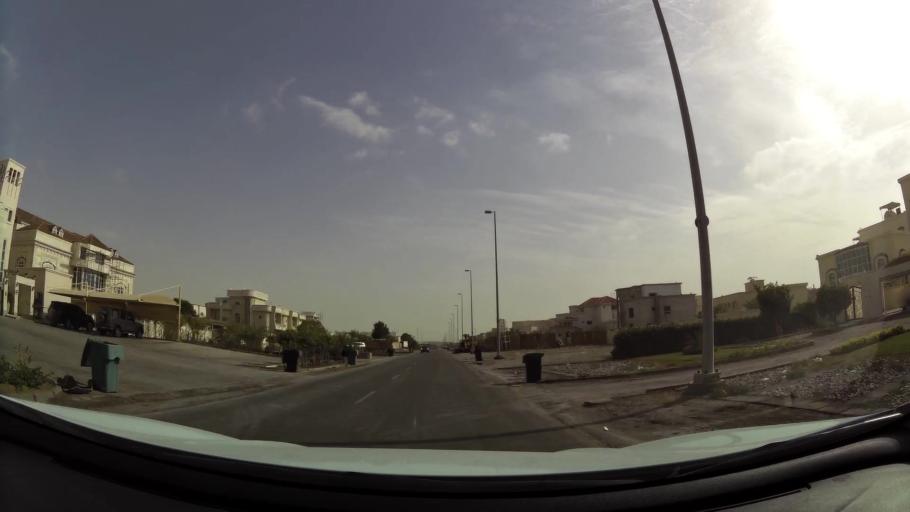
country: AE
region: Abu Dhabi
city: Abu Dhabi
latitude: 24.4140
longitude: 54.5773
